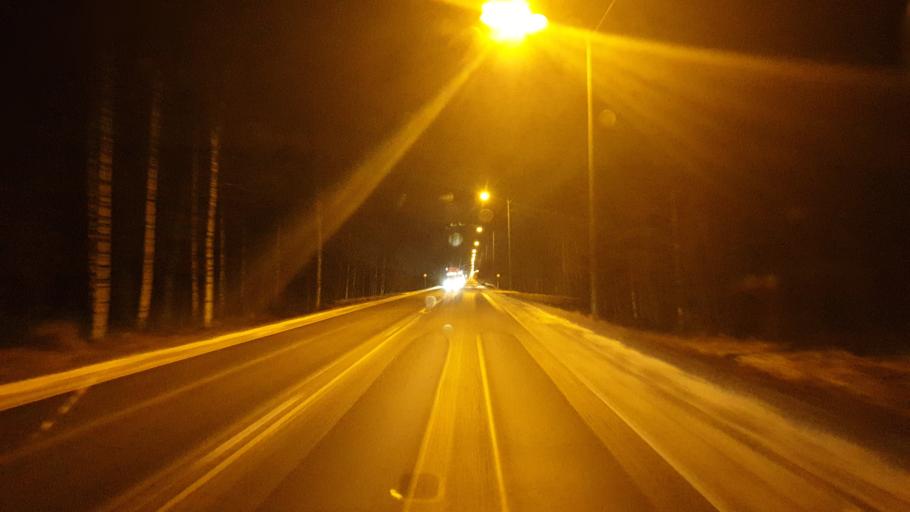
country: FI
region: Central Finland
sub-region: AEaenekoski
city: AEaenekoski
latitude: 62.4726
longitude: 25.6712
